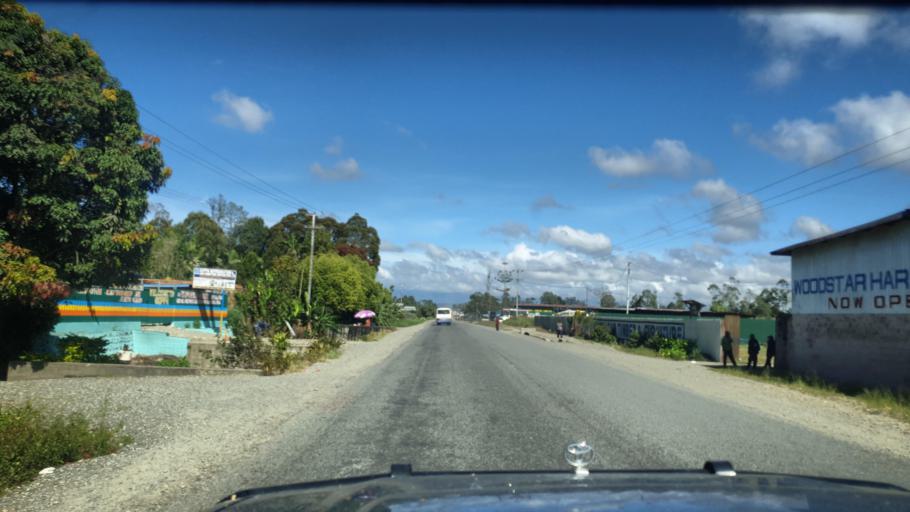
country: PG
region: Western Highlands
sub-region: Hagen
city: Mount Hagen
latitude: -5.8401
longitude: 144.3068
